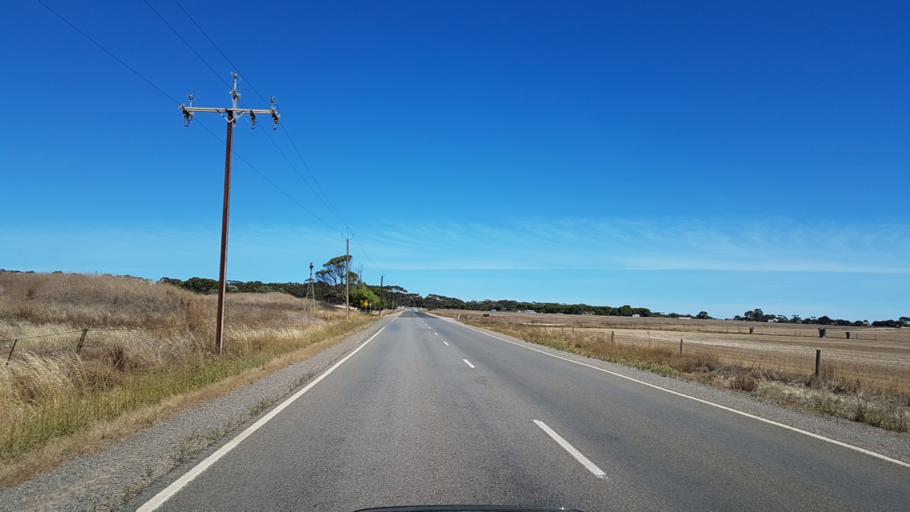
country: AU
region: South Australia
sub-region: Yorke Peninsula
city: Maitland
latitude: -34.3622
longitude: 137.6673
